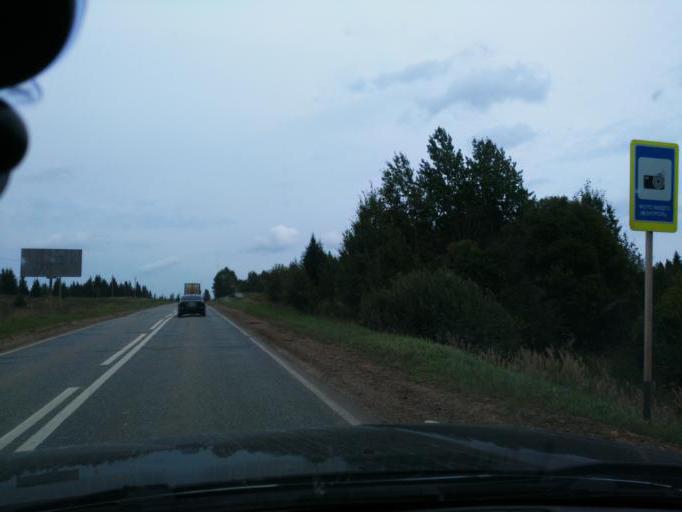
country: RU
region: Bashkortostan
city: Verkhniye Tatyshly
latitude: 56.4939
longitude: 55.8219
